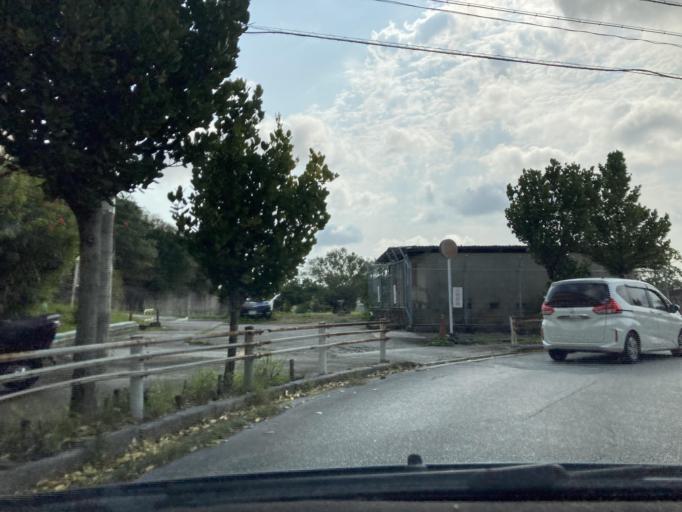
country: JP
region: Okinawa
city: Tomigusuku
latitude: 26.1984
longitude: 127.7211
